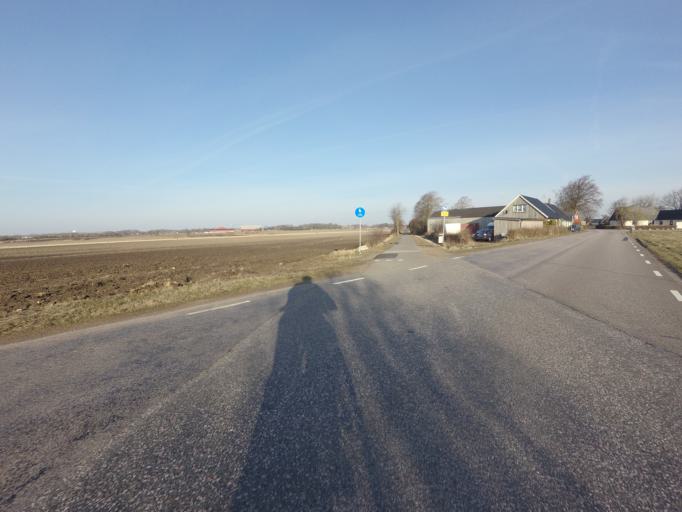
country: SE
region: Skane
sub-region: Hoganas Kommun
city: Hoganas
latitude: 56.1954
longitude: 12.6020
